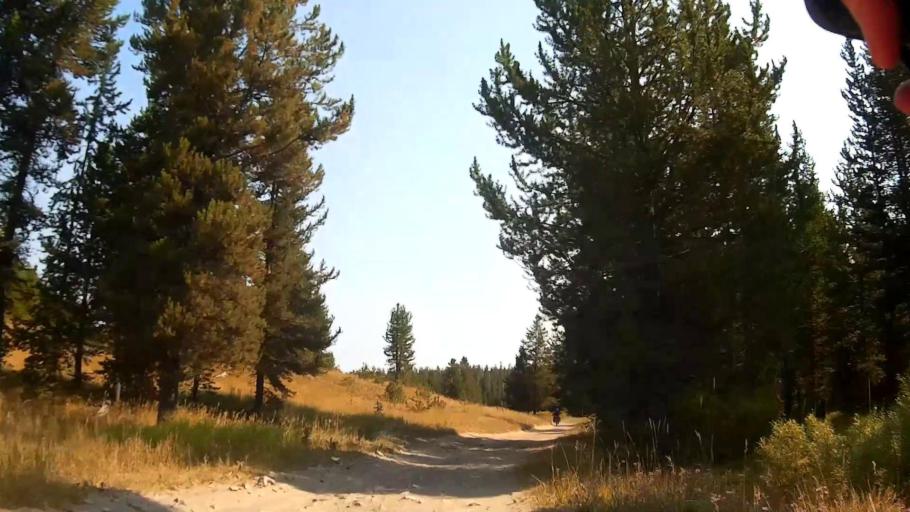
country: US
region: Montana
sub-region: Gallatin County
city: West Yellowstone
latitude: 44.5753
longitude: -111.1846
